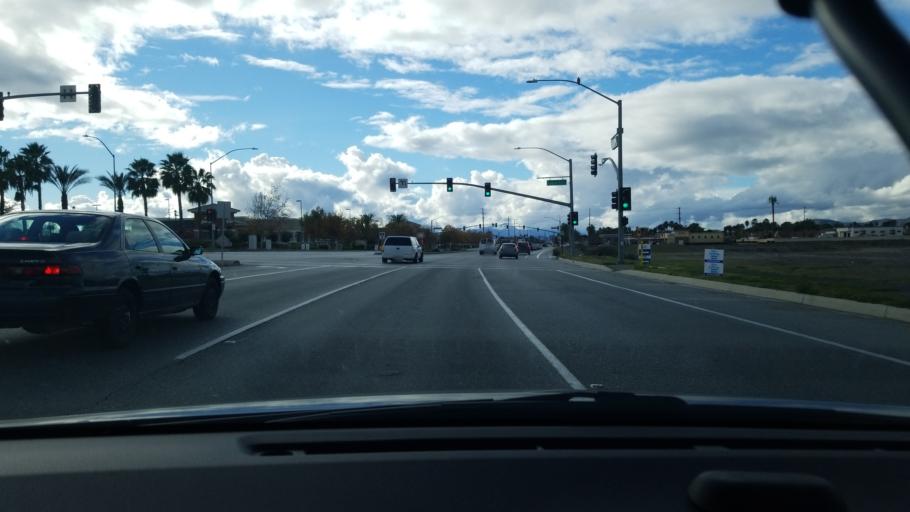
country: US
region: California
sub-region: Riverside County
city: Menifee
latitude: 33.6852
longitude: -117.1490
